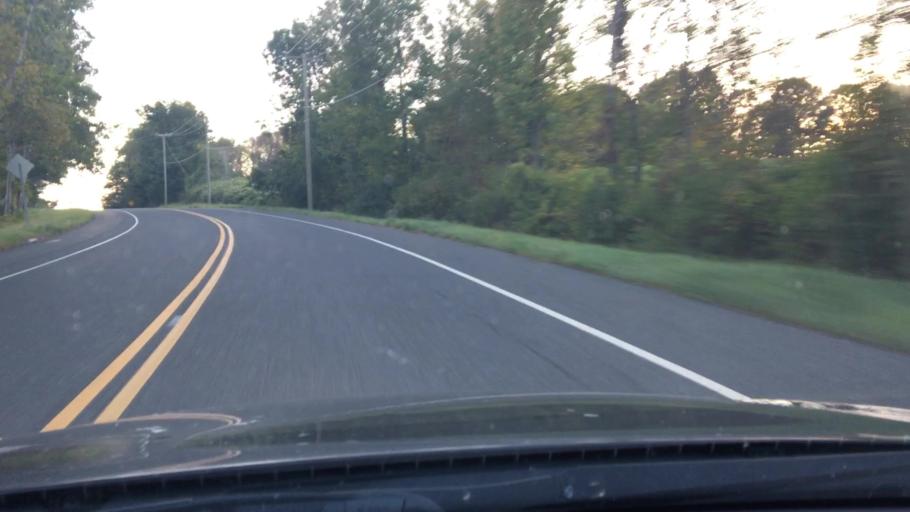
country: US
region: Connecticut
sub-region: Litchfield County
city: Bethlehem Village
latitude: 41.6784
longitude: -73.2553
